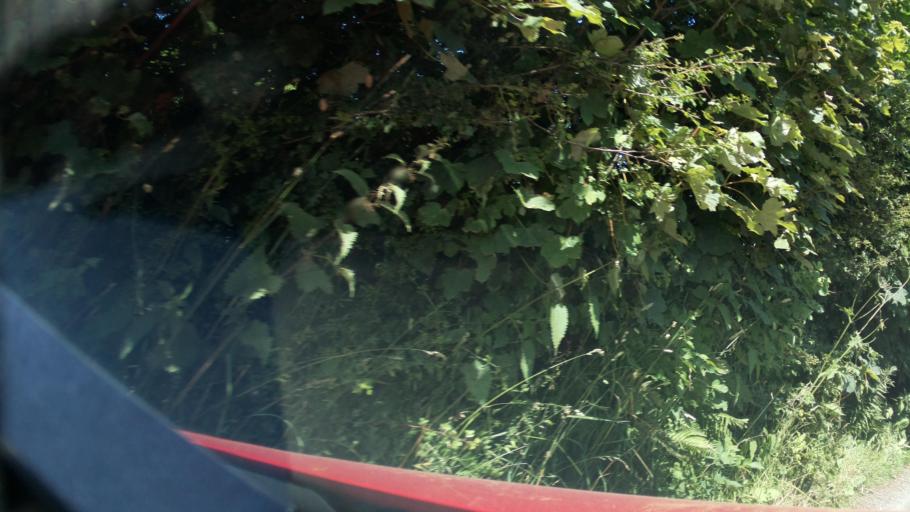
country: GB
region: England
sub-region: Derbyshire
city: Buxton
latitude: 53.1932
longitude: -1.8790
